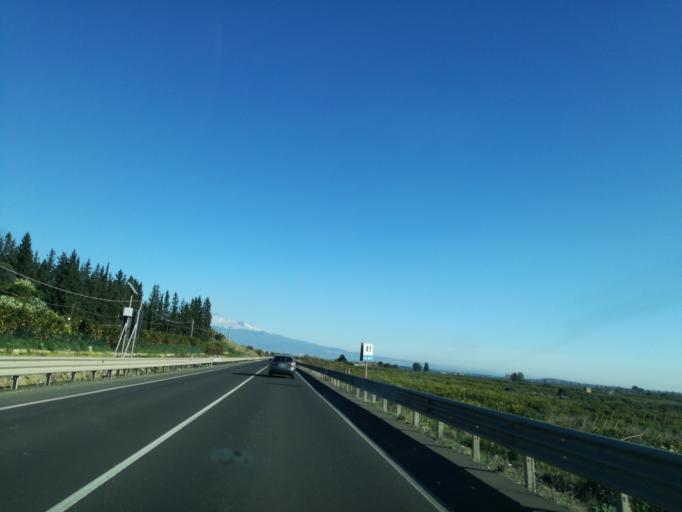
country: IT
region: Sicily
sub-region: Catania
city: Ramacca
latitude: 37.3725
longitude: 14.7258
